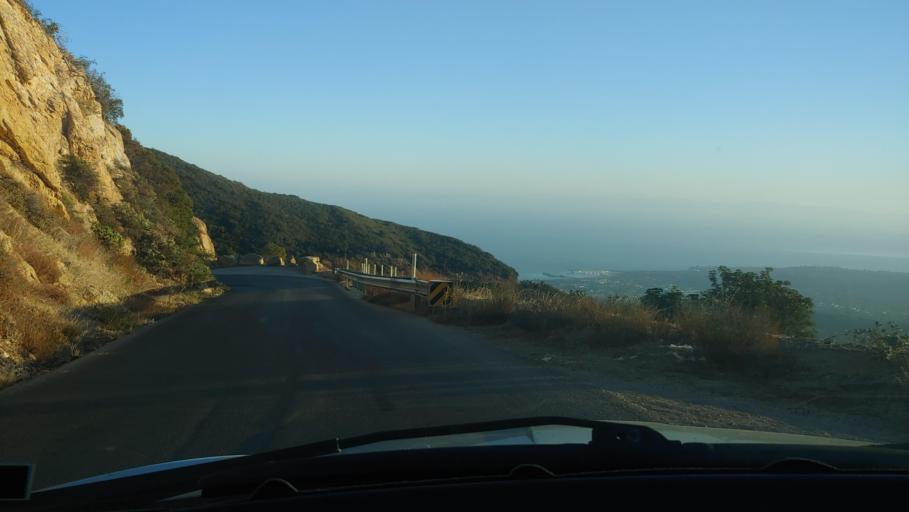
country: US
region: California
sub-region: Santa Barbara County
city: Mission Canyon
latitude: 34.4789
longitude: -119.6812
